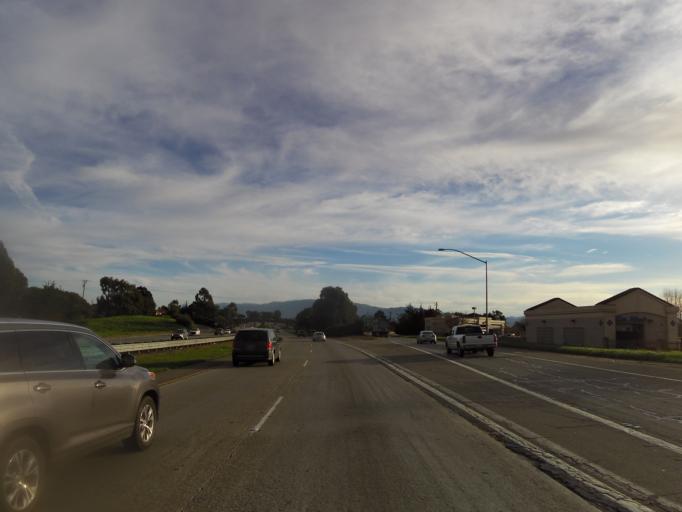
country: US
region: California
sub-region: Monterey County
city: Boronda
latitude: 36.7018
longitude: -121.6664
